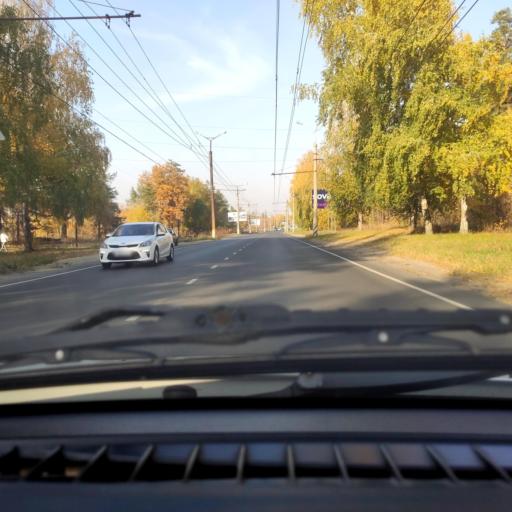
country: RU
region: Samara
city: Tol'yatti
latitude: 53.4925
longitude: 49.3859
